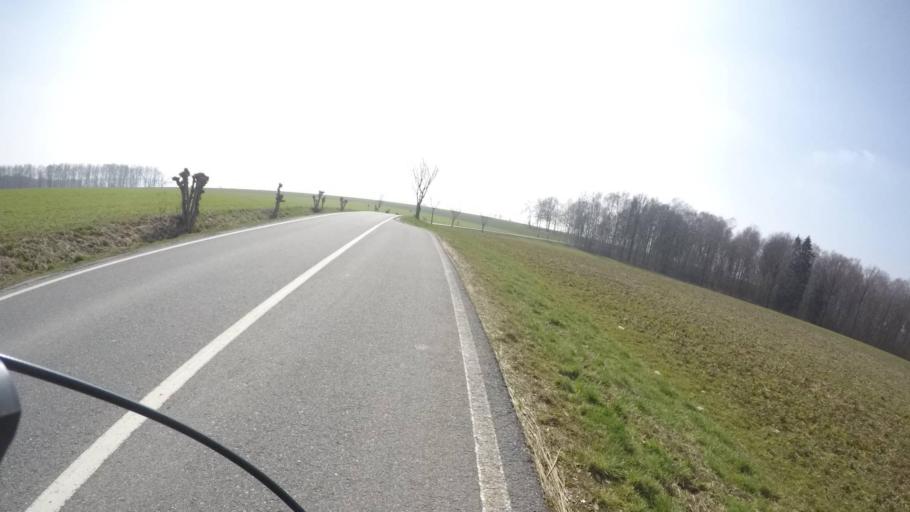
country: DE
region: Saxony
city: Niederfrohna
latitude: 50.8630
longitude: 12.6912
